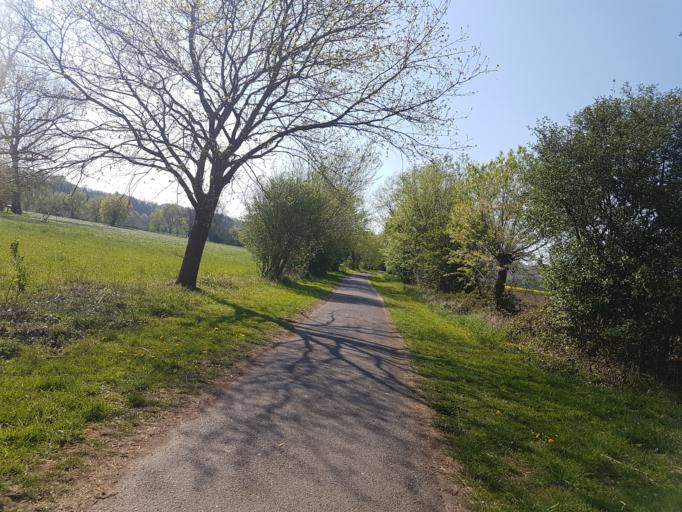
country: DE
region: North Rhine-Westphalia
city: Hattingen
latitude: 51.4166
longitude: 7.2253
